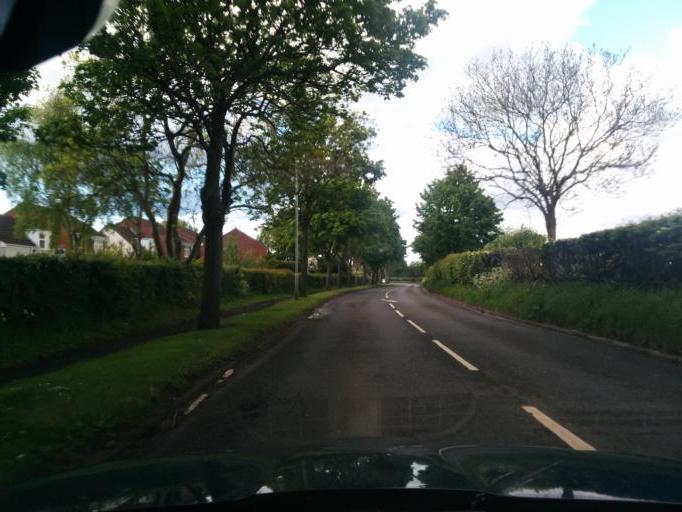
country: GB
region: England
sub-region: Northumberland
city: Bedlington
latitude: 55.1373
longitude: -1.5990
